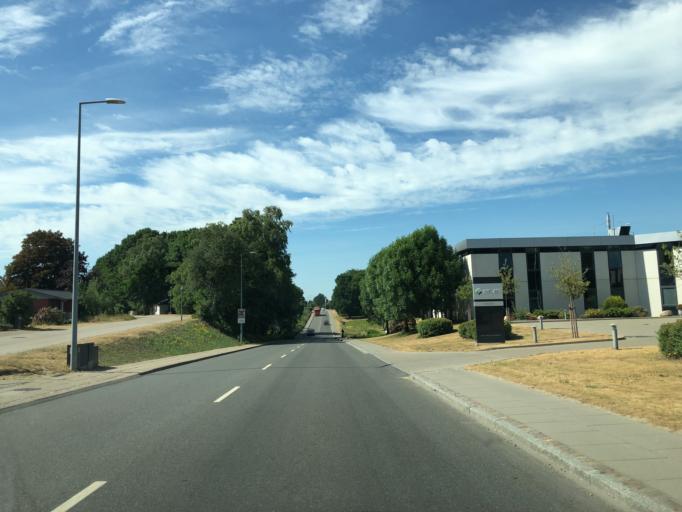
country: DK
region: Central Jutland
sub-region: Ikast-Brande Kommune
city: Brande
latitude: 55.9504
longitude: 9.1177
